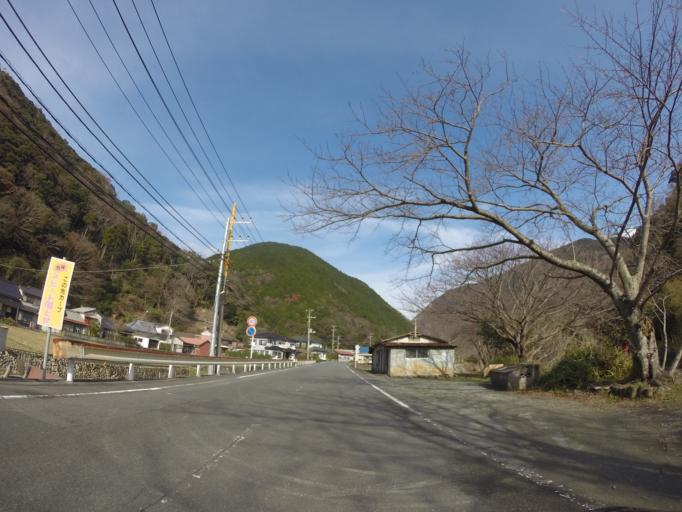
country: JP
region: Shizuoka
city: Heda
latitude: 34.7905
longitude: 138.8016
